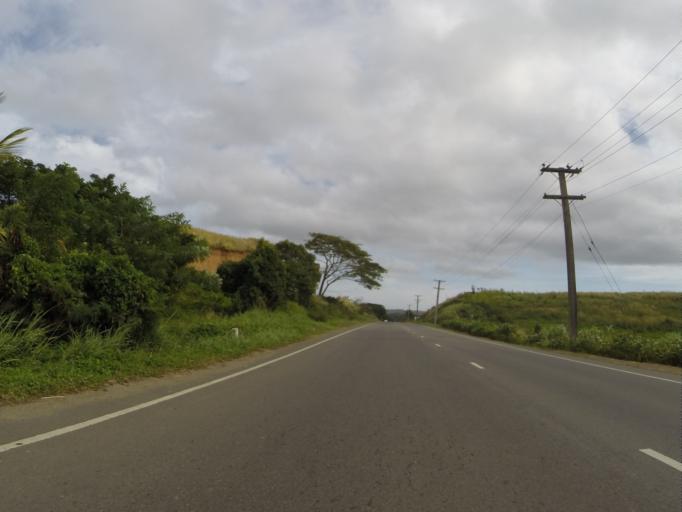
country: FJ
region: Western
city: Nadi
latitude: -18.1585
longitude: 177.5195
